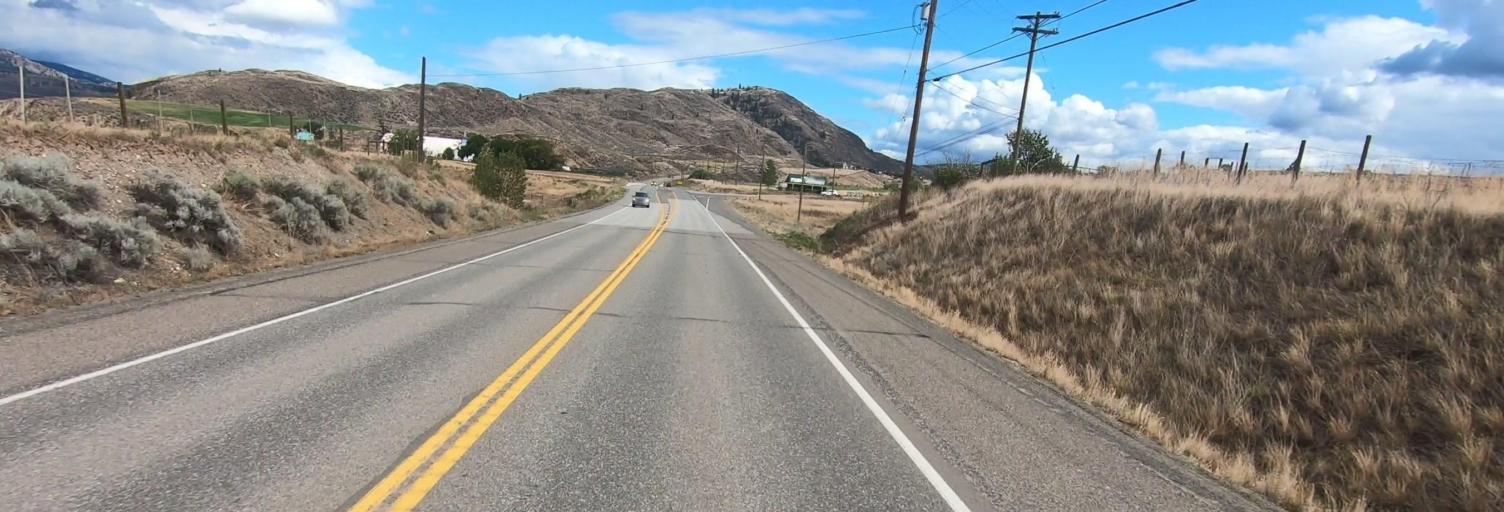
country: CA
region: British Columbia
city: Logan Lake
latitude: 50.7177
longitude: -120.6430
